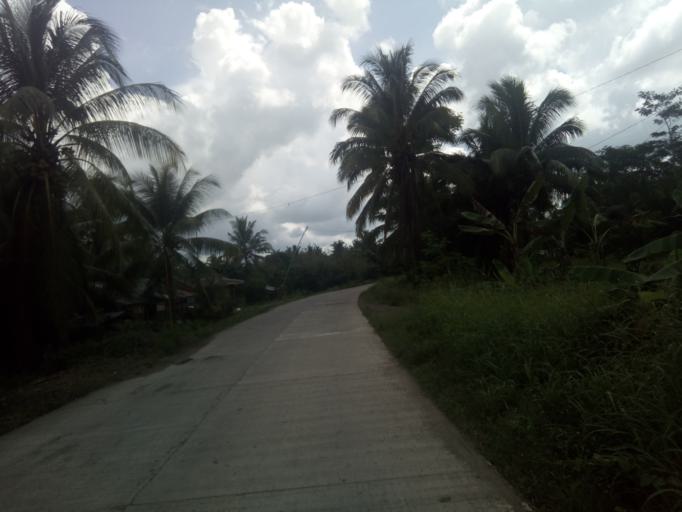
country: PH
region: Caraga
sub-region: Province of Agusan del Sur
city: Santa Josefa
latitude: 7.9934
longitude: 126.0295
